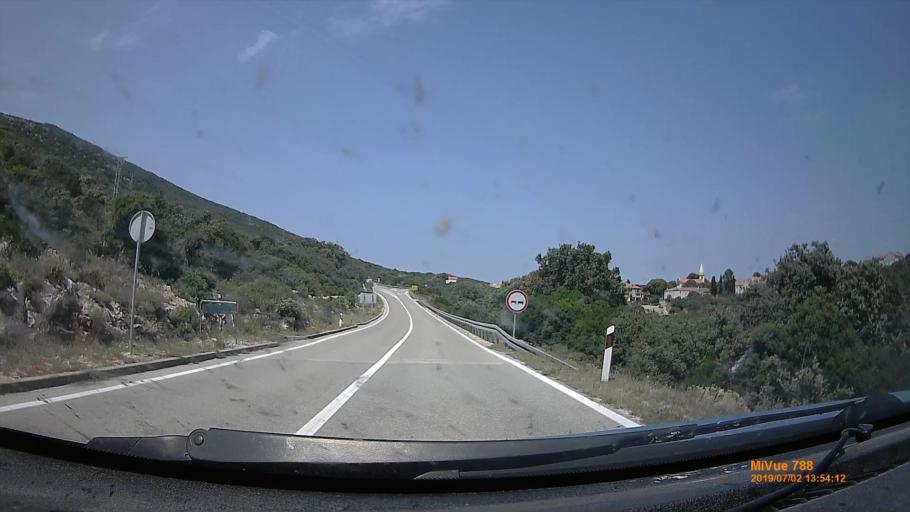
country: HR
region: Primorsko-Goranska
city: Mali Losinj
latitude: 44.6363
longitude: 14.3919
